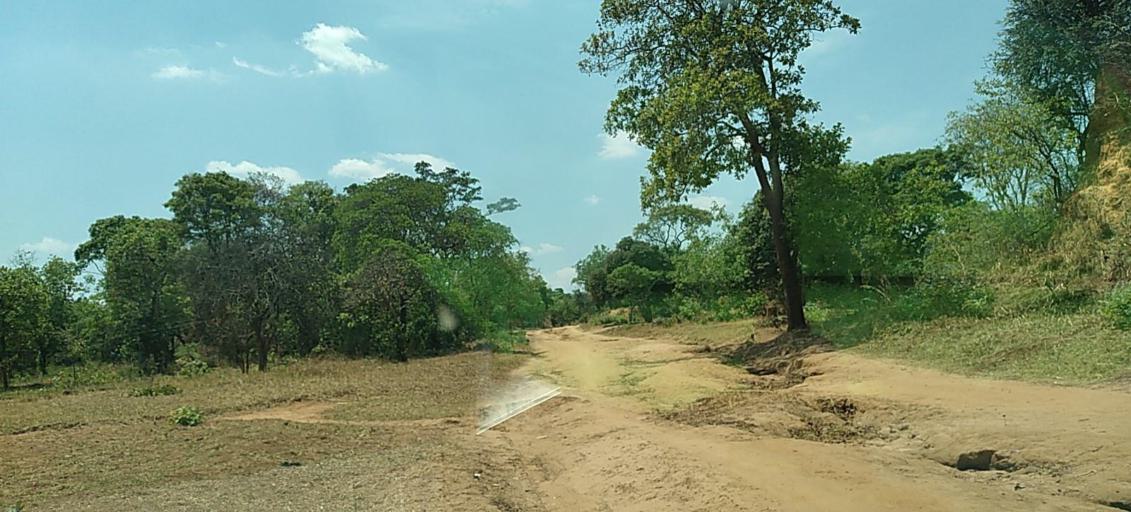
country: CD
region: Katanga
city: Kolwezi
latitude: -11.3249
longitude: 25.2286
